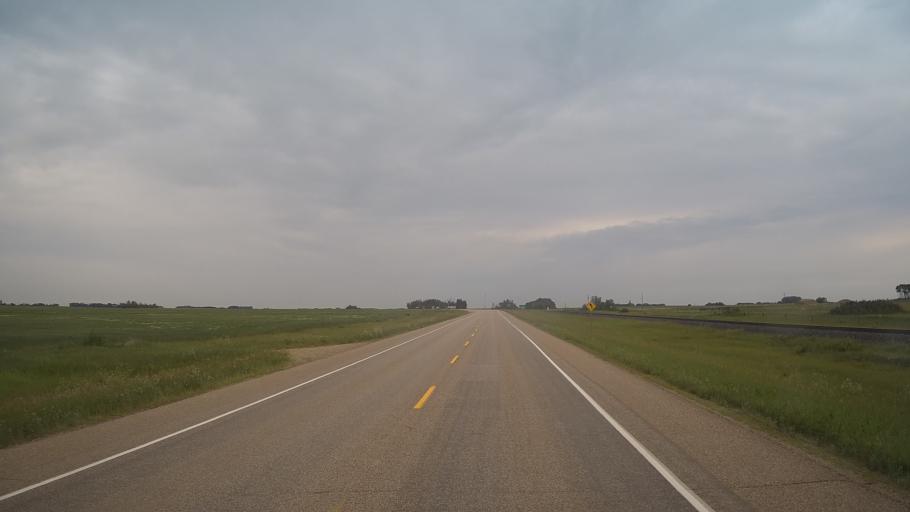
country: CA
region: Saskatchewan
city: Langham
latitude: 52.1265
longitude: -107.2819
